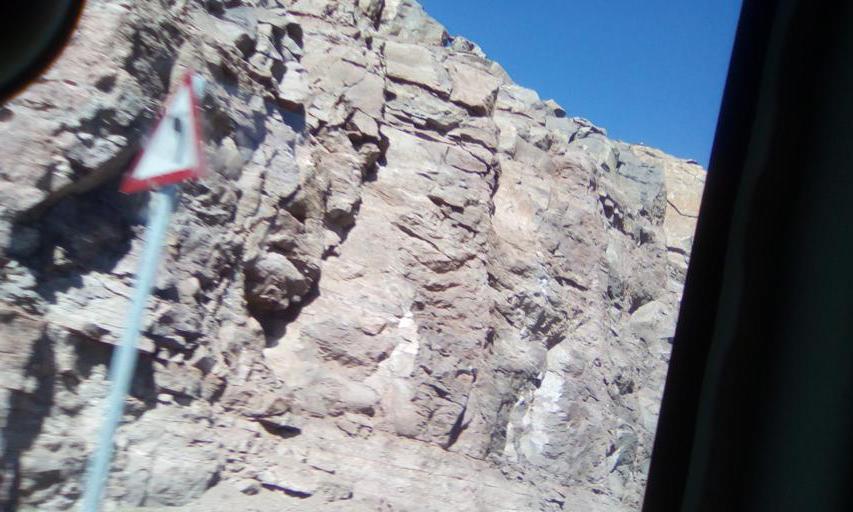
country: LS
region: Maseru
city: Nako
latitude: -29.8906
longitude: 28.1167
